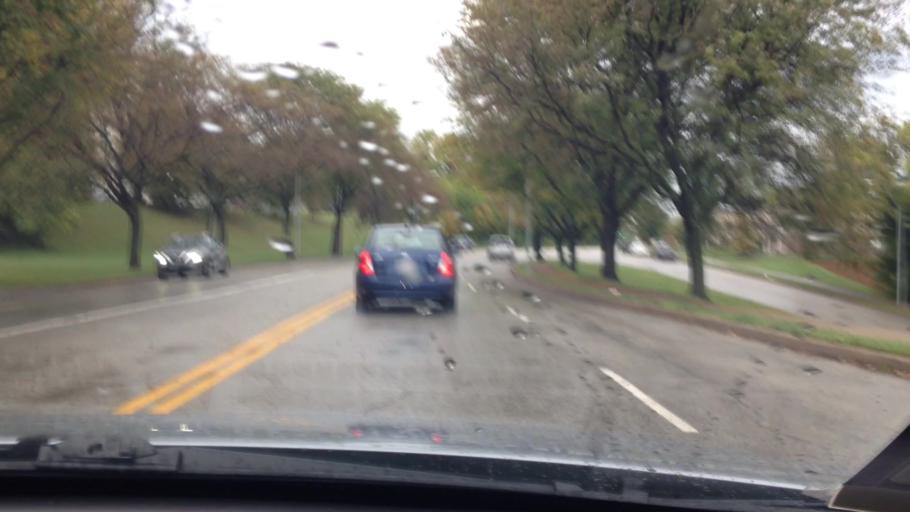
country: US
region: Missouri
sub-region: Jackson County
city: Kansas City
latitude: 39.0777
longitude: -94.5652
